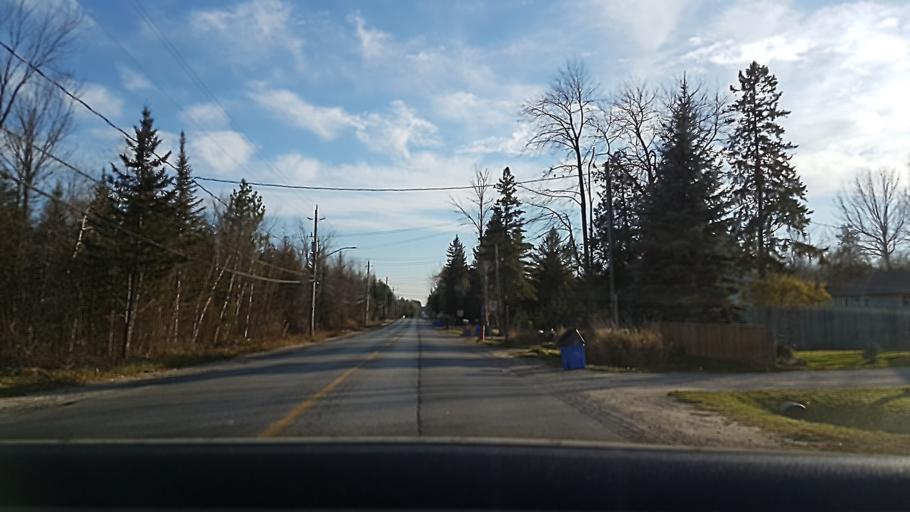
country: CA
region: Ontario
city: Innisfil
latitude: 44.3397
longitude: -79.5457
